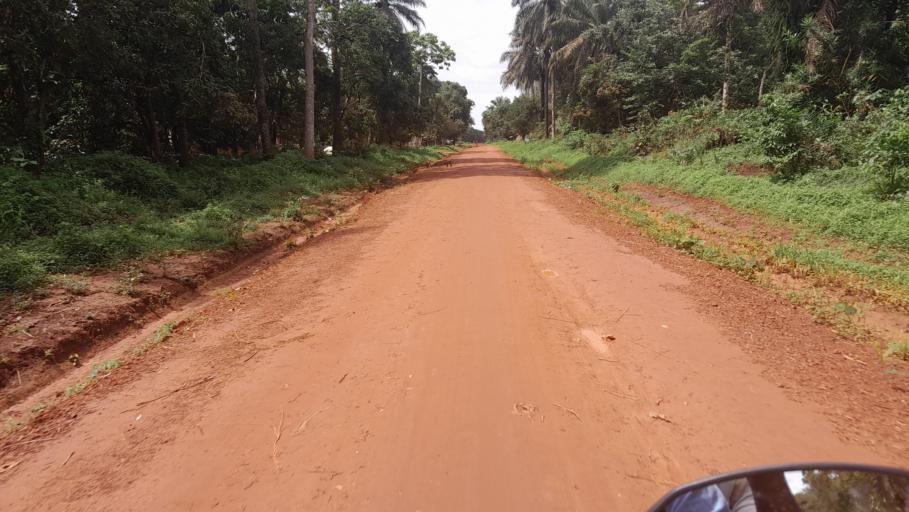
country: GN
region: Boke
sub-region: Boffa
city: Boffa
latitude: 10.0168
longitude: -13.8887
